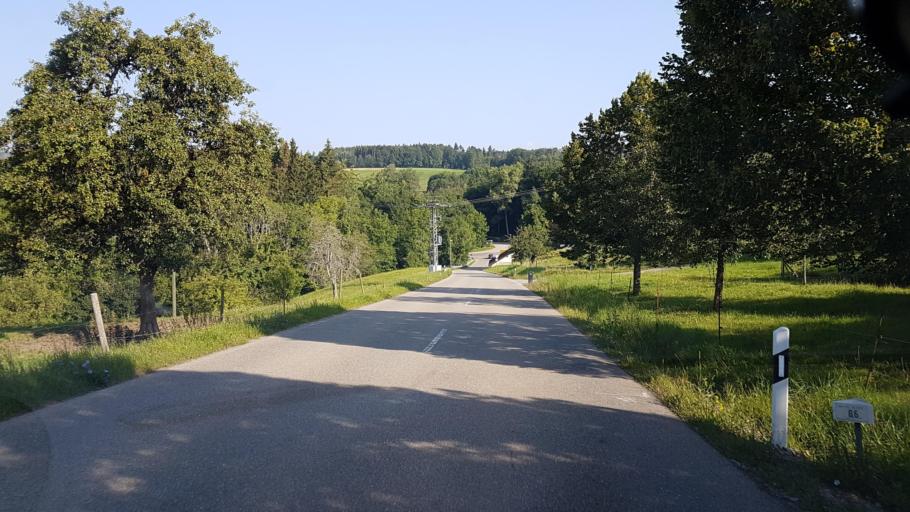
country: DE
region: Baden-Wuerttemberg
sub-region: Freiburg Region
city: Gorwihl
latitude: 47.6297
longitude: 8.1103
